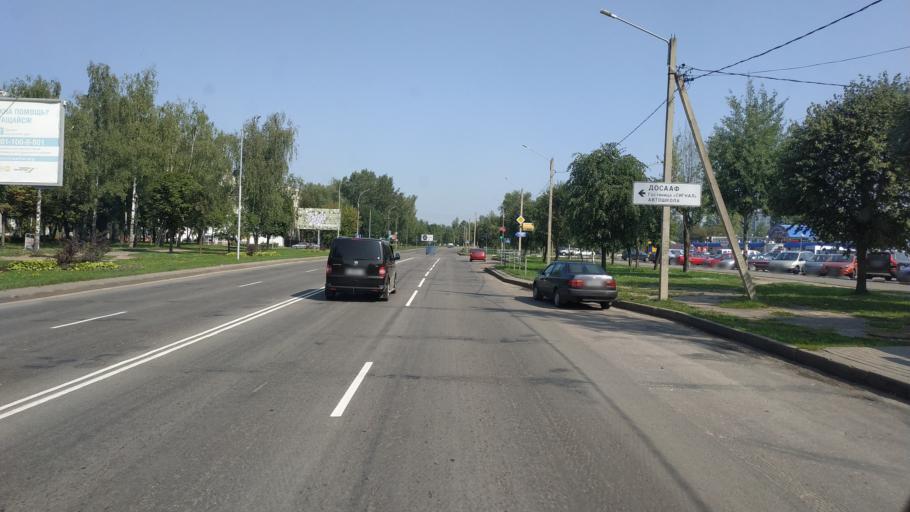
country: BY
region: Mogilev
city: Buynichy
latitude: 53.8721
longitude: 30.3130
